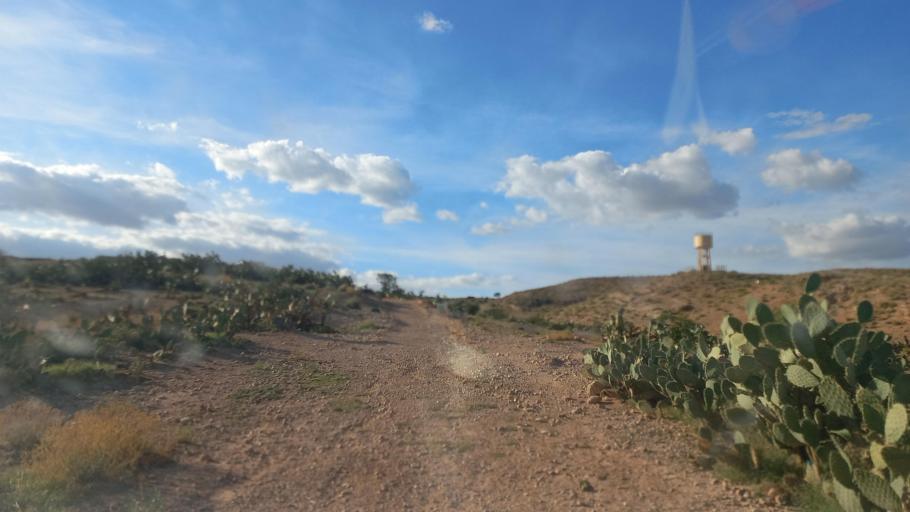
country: TN
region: Al Qasrayn
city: Sbiba
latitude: 35.3819
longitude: 9.0204
